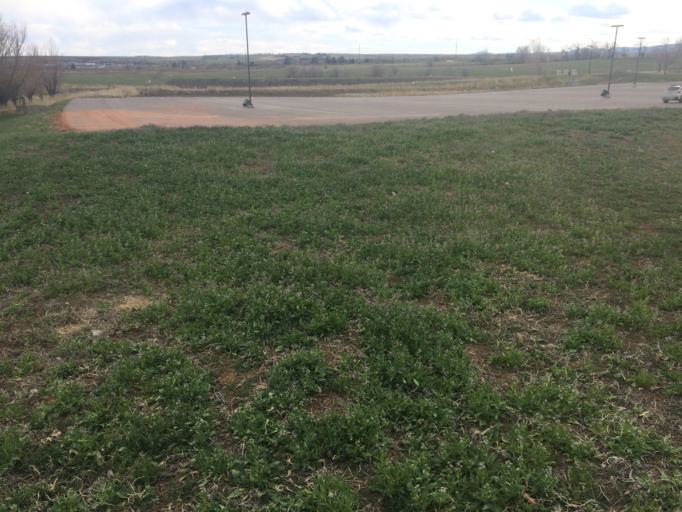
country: US
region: Colorado
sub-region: Boulder County
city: Louisville
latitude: 39.9520
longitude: -105.1379
